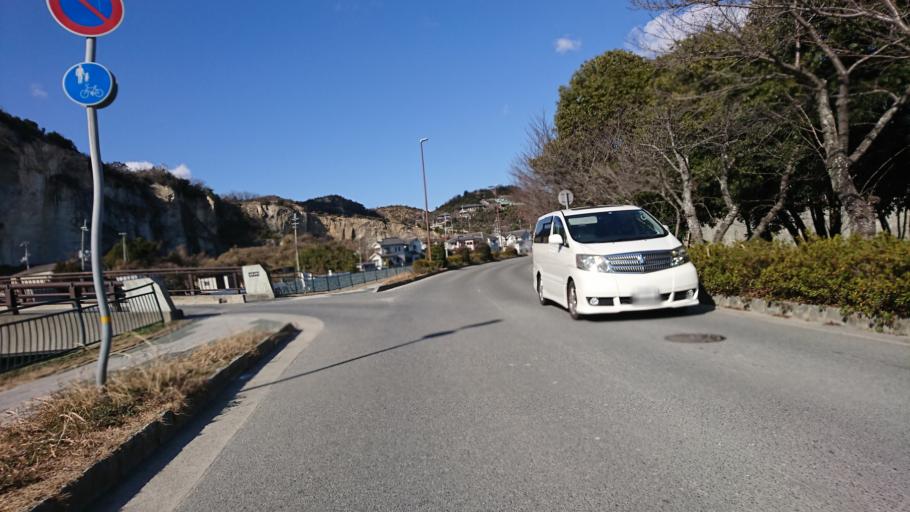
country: JP
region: Hyogo
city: Kakogawacho-honmachi
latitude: 34.7793
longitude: 134.7985
